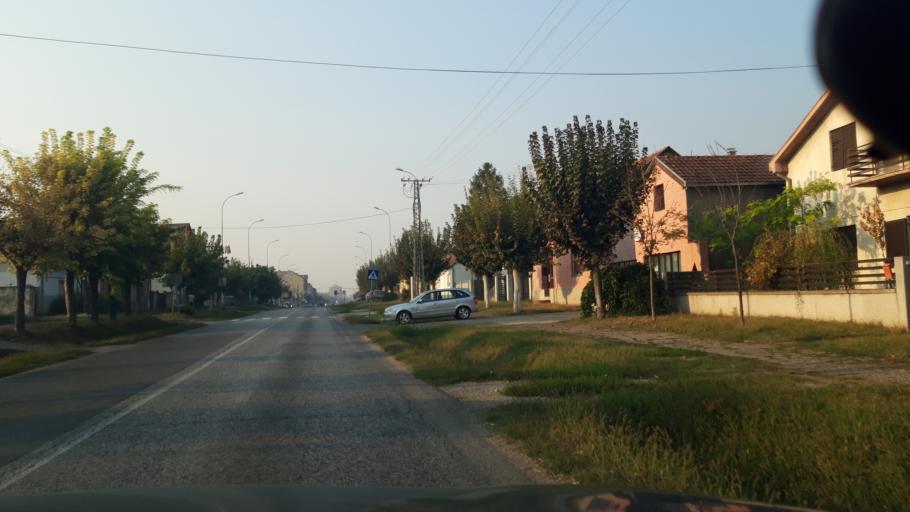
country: RS
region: Autonomna Pokrajina Vojvodina
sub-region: Sremski Okrug
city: Ingija
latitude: 45.0393
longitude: 20.0899
